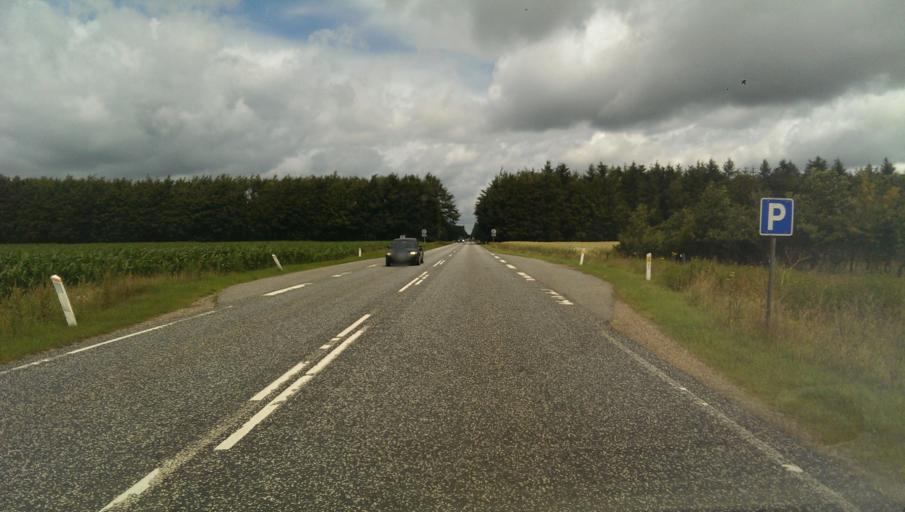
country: DK
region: Central Jutland
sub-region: Ikast-Brande Kommune
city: Bording Kirkeby
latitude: 56.0321
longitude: 9.3770
